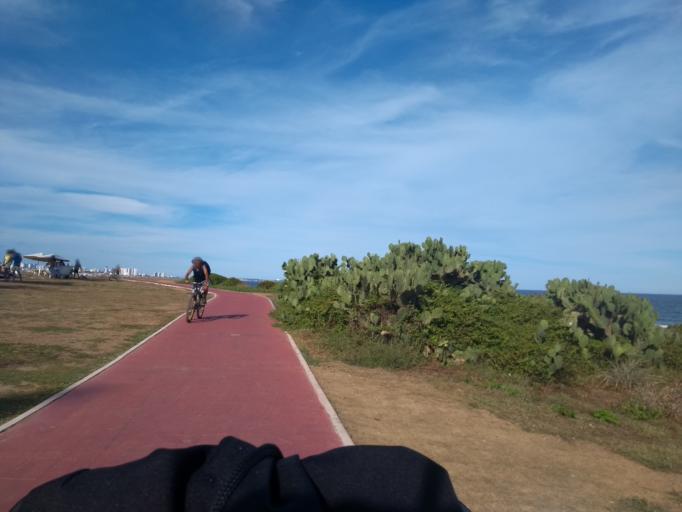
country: BR
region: Bahia
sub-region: Salvador
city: Salvador
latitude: -12.9969
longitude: -38.4422
